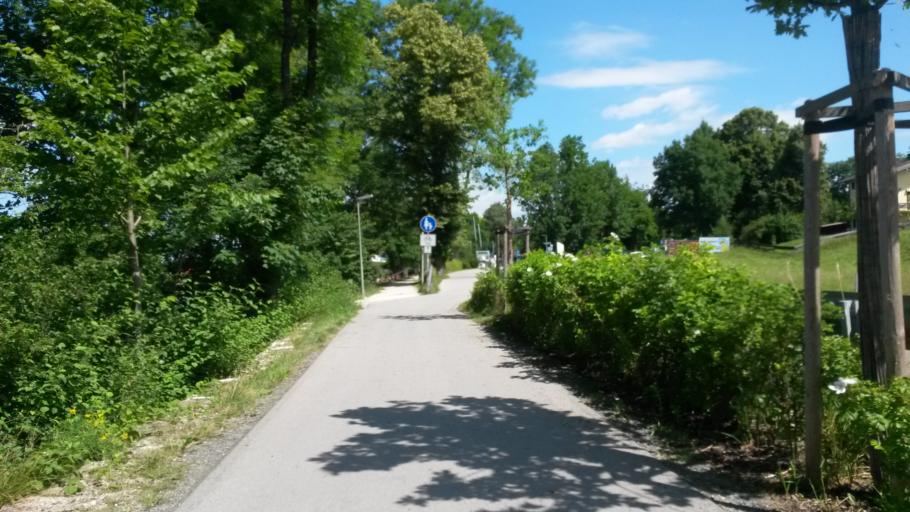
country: DE
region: Bavaria
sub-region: Upper Bavaria
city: Chieming
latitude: 47.8847
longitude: 12.5341
